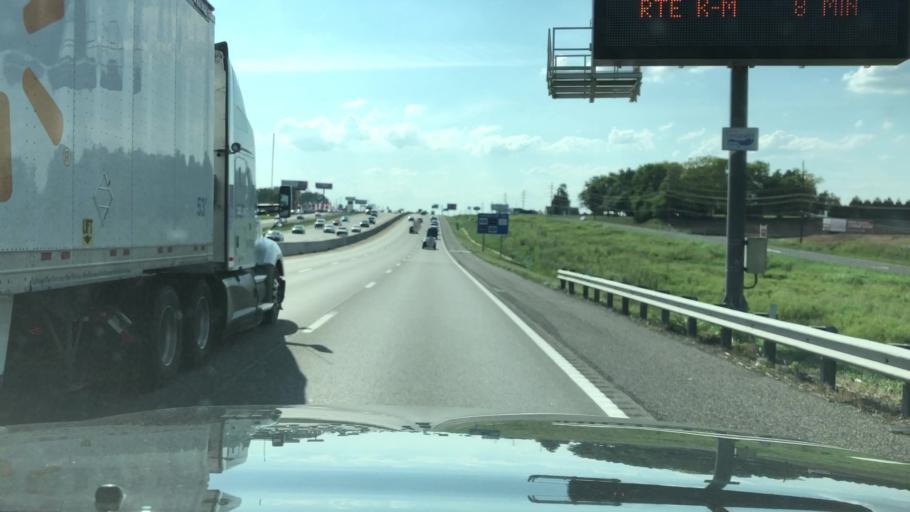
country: US
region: Missouri
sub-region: Saint Charles County
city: Saint Charles
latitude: 38.7900
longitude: -90.5500
